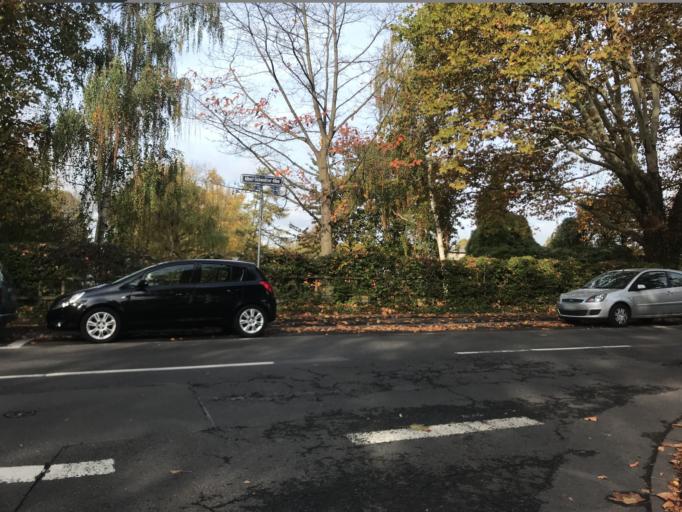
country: DE
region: Hesse
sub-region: Regierungsbezirk Darmstadt
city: Wiesbaden
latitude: 50.0419
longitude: 8.2279
